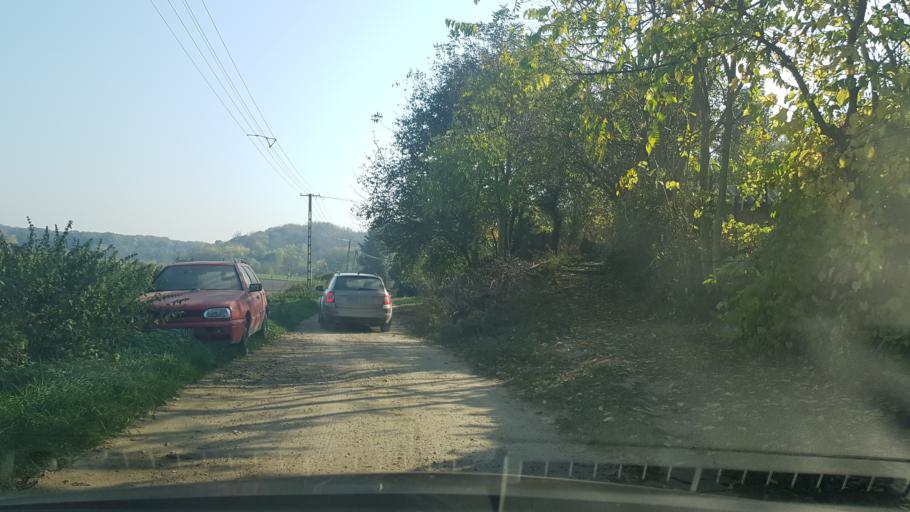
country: HU
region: Fejer
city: Adony
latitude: 47.0754
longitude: 18.8615
